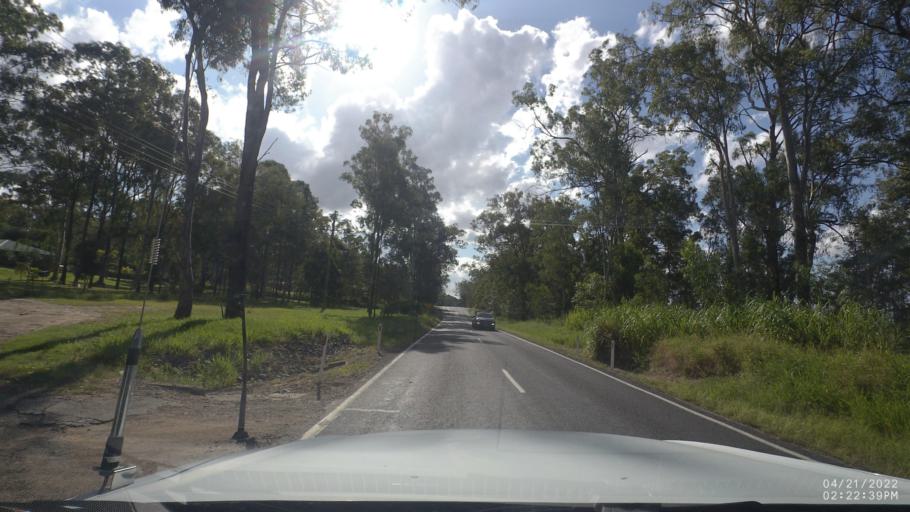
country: AU
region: Queensland
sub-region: Logan
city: Chambers Flat
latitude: -27.8236
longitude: 153.1022
